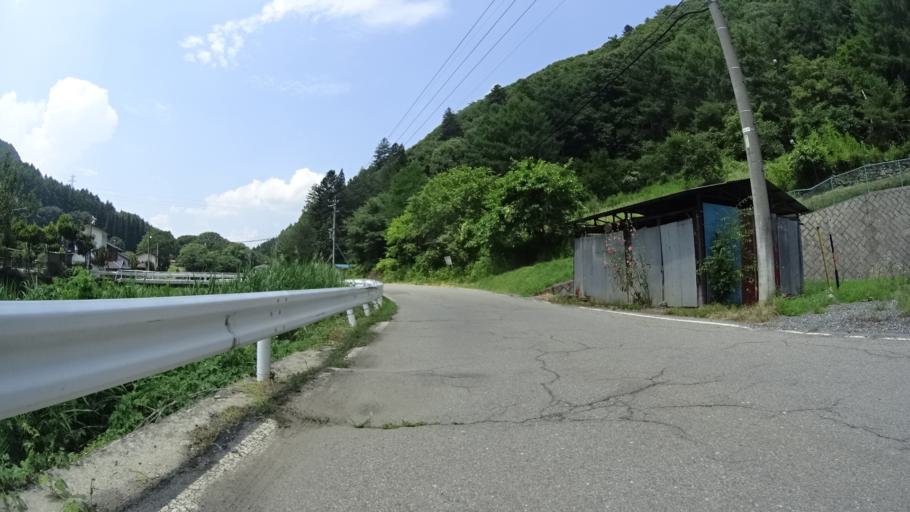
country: JP
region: Nagano
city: Saku
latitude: 36.1289
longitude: 138.5797
